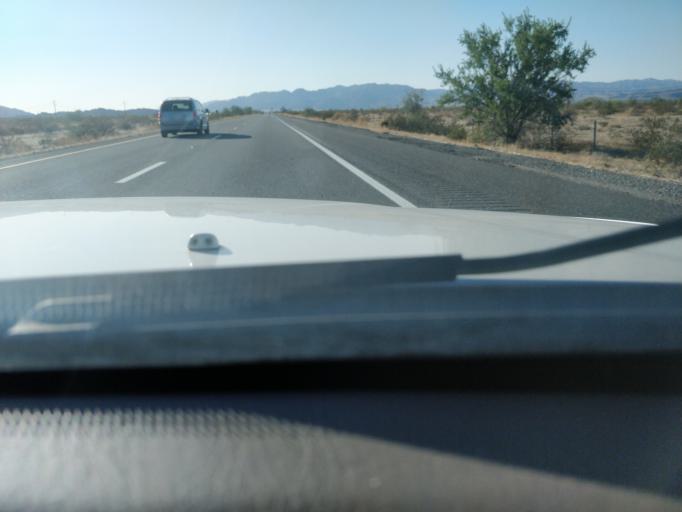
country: US
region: California
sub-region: Imperial County
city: Niland
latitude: 33.7077
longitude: -115.3549
